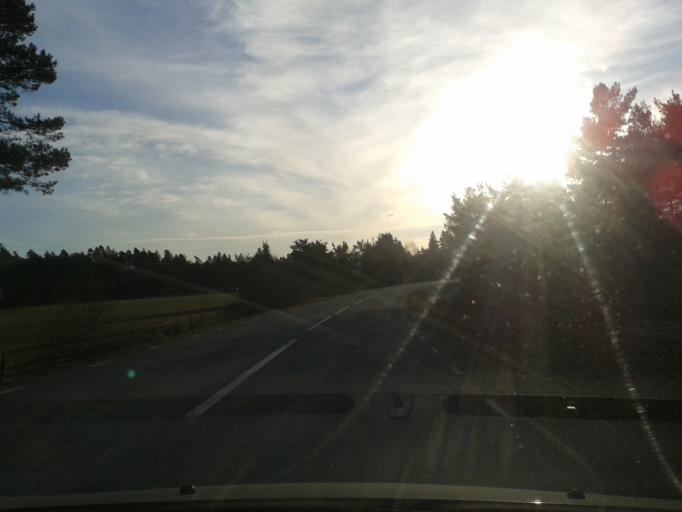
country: SE
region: Gotland
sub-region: Gotland
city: Hemse
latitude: 57.3451
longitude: 18.6930
